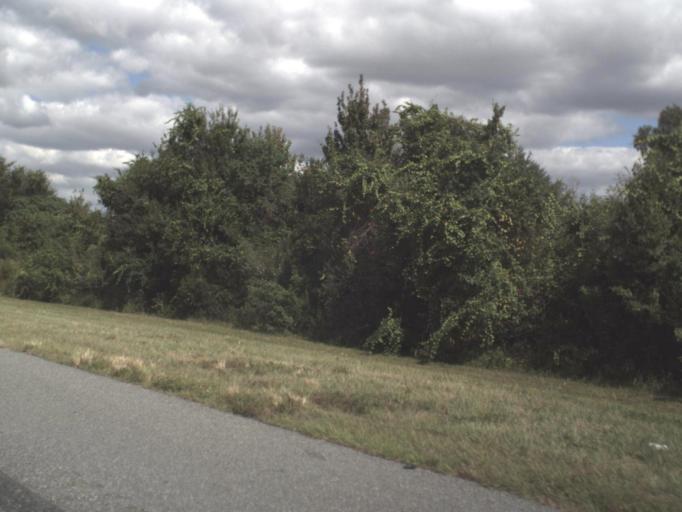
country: US
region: Florida
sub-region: Orange County
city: Southchase
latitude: 28.4200
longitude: -81.3930
